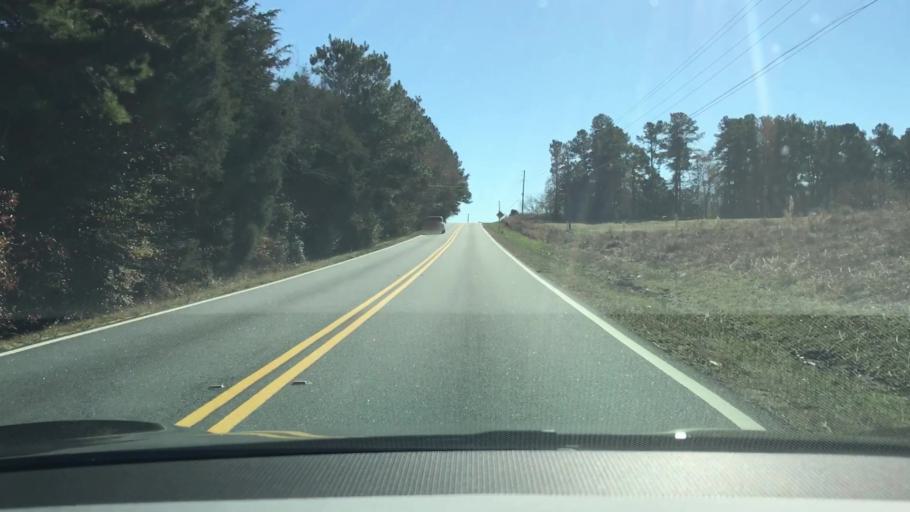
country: US
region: Georgia
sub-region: Barrow County
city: Auburn
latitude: 33.9085
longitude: -83.8154
